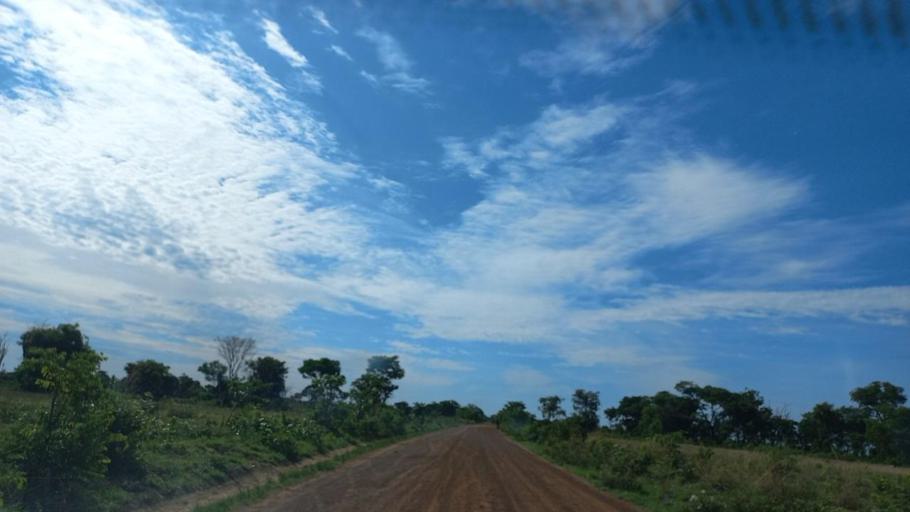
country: ZM
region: North-Western
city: Kabompo
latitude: -13.4325
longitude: 24.4190
